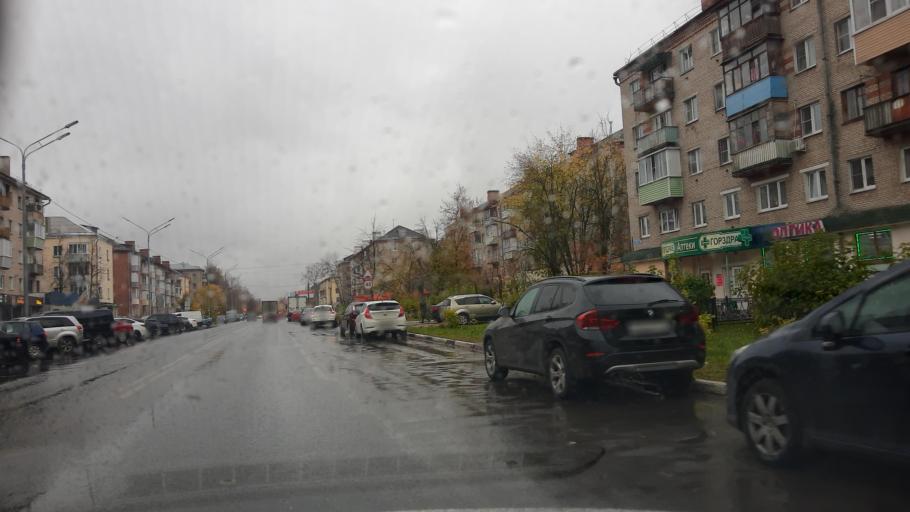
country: RU
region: Moskovskaya
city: Elektrostal'
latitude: 55.8002
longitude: 38.4378
